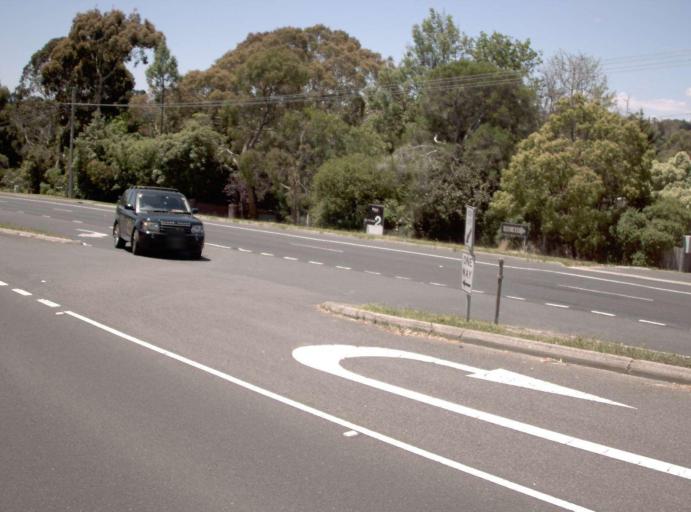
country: AU
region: Victoria
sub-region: Mornington Peninsula
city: Mount Eliza
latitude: -38.1869
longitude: 145.0960
